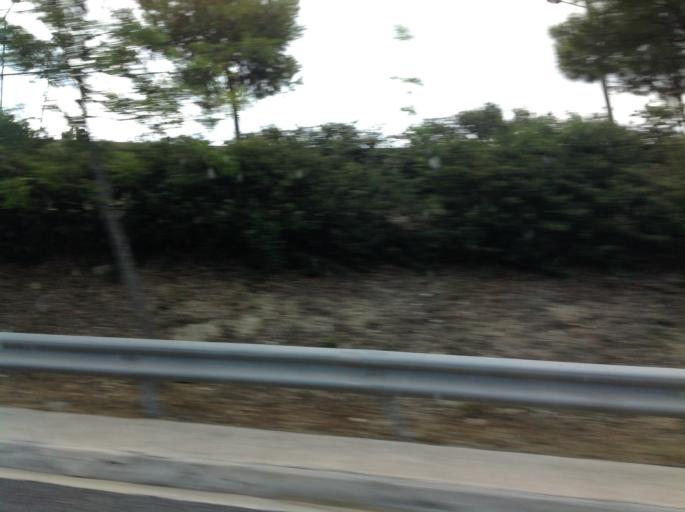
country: GR
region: Attica
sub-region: Nomarchia Anatolikis Attikis
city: Leondarion
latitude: 37.9975
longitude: 23.8510
